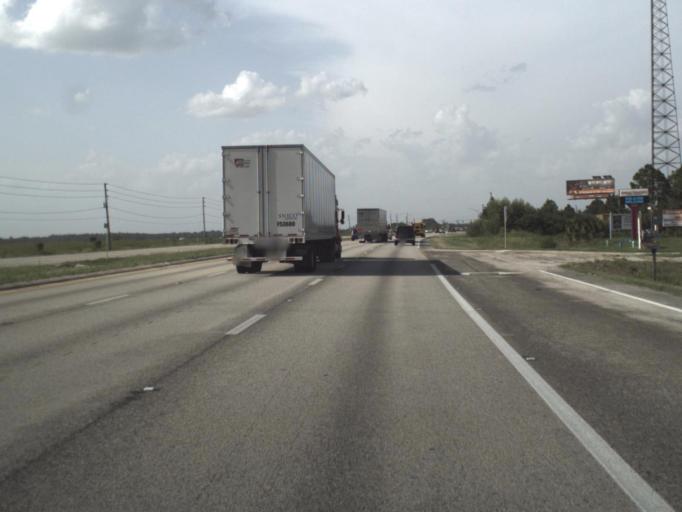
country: US
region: Florida
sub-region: Polk County
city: Dundee
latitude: 27.9733
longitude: -81.6298
